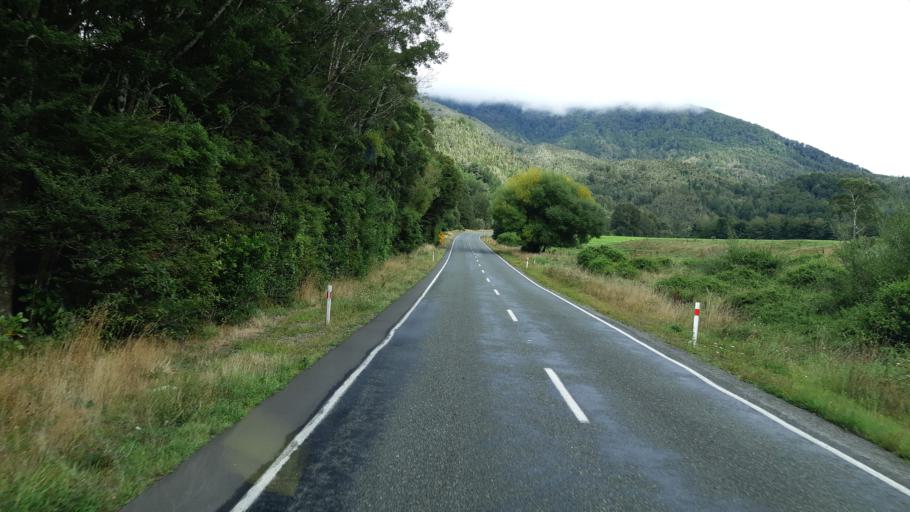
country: NZ
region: West Coast
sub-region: Buller District
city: Westport
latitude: -41.8093
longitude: 172.2237
